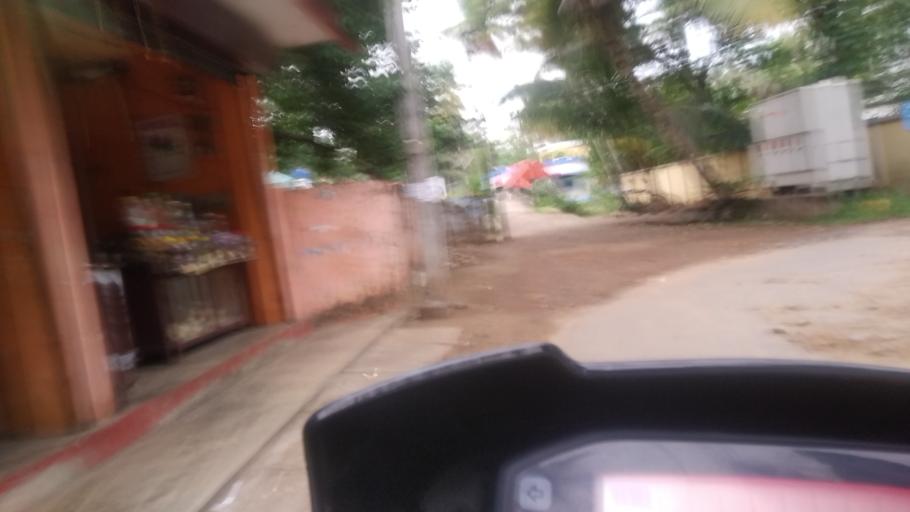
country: IN
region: Kerala
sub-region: Ernakulam
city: Elur
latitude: 10.0676
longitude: 76.2172
